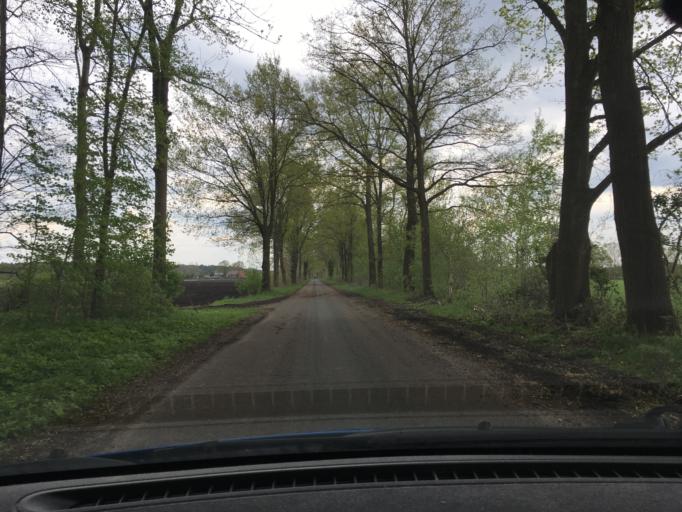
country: DE
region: Lower Saxony
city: Radbruch
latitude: 53.2937
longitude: 10.2659
